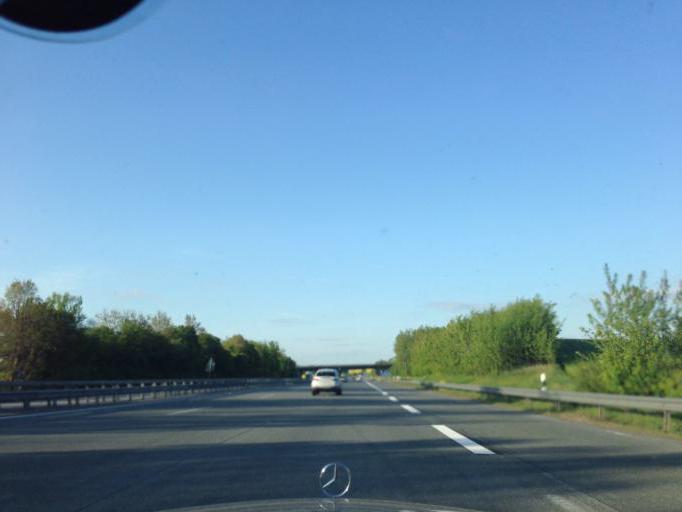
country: DE
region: Schleswig-Holstein
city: Politz
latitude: 53.7818
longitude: 10.4144
